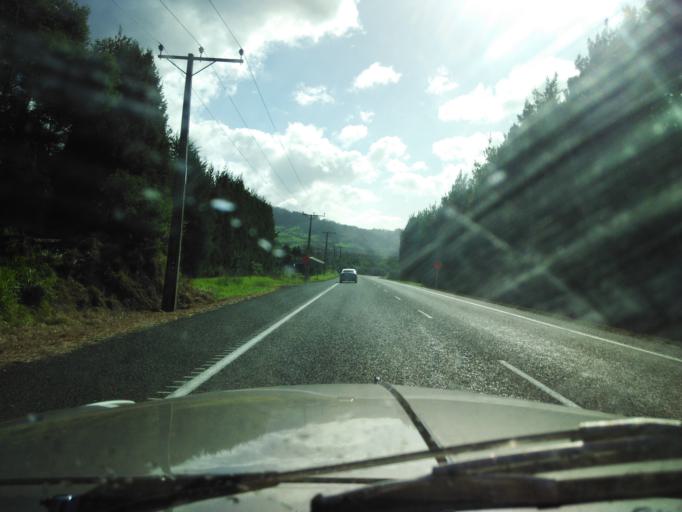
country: NZ
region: Bay of Plenty
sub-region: Western Bay of Plenty District
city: Katikati
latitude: -37.5158
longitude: 175.9193
